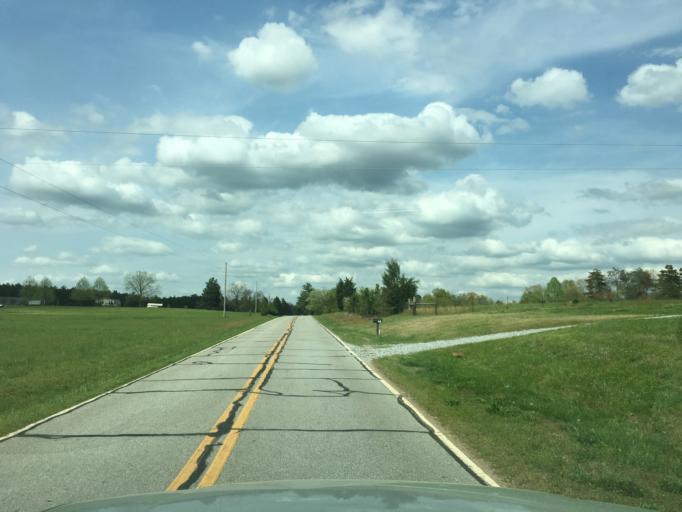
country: US
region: North Carolina
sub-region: Rutherford County
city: Spindale
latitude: 35.2123
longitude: -81.9707
